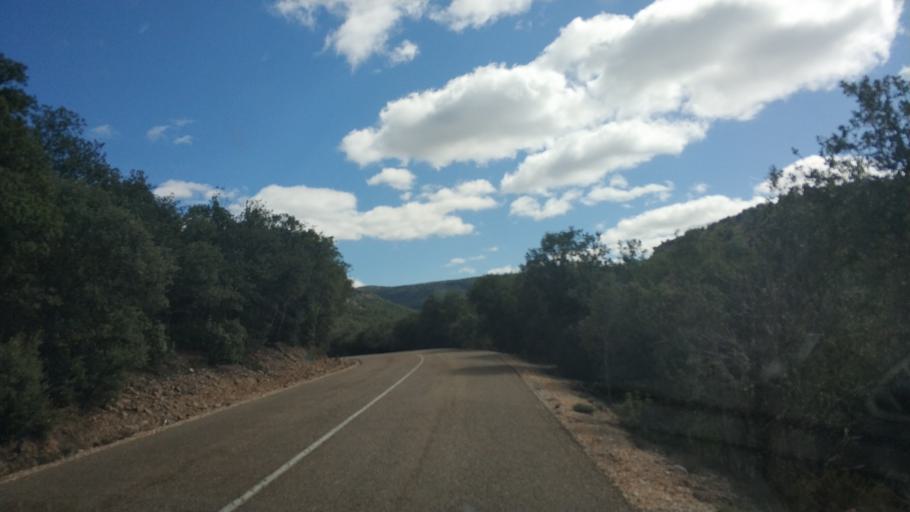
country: ES
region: Castille and Leon
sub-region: Provincia de Burgos
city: Retuerta
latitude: 42.0375
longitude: -3.4836
